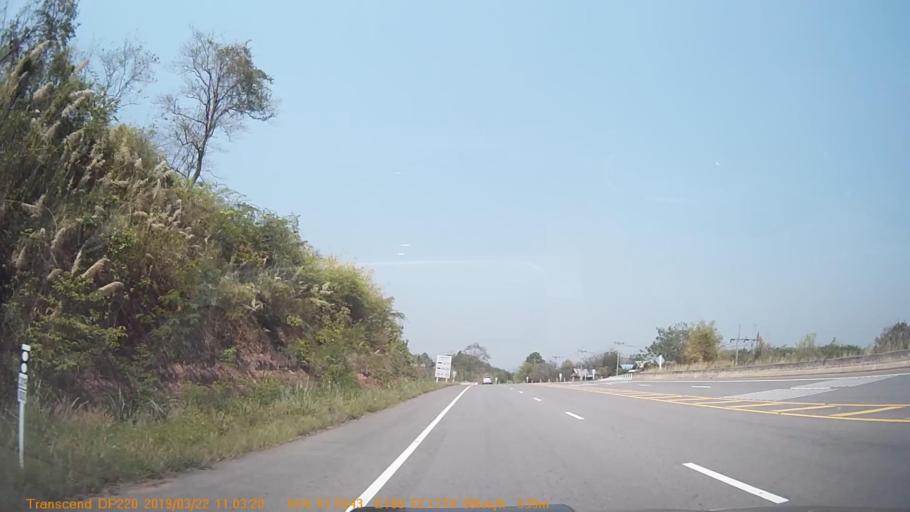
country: TH
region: Phitsanulok
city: Nakhon Thai
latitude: 16.8593
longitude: 100.8700
